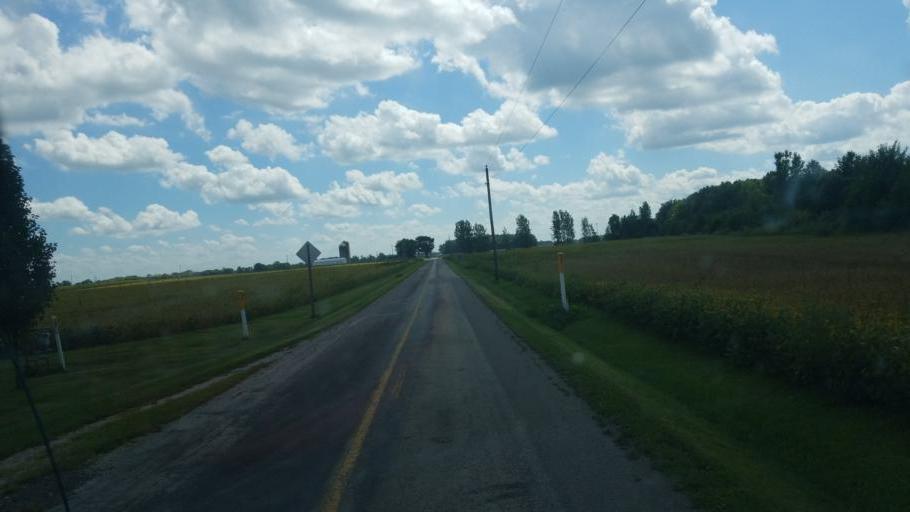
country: US
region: Ohio
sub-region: Marion County
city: Prospect
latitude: 40.4886
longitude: -83.1664
